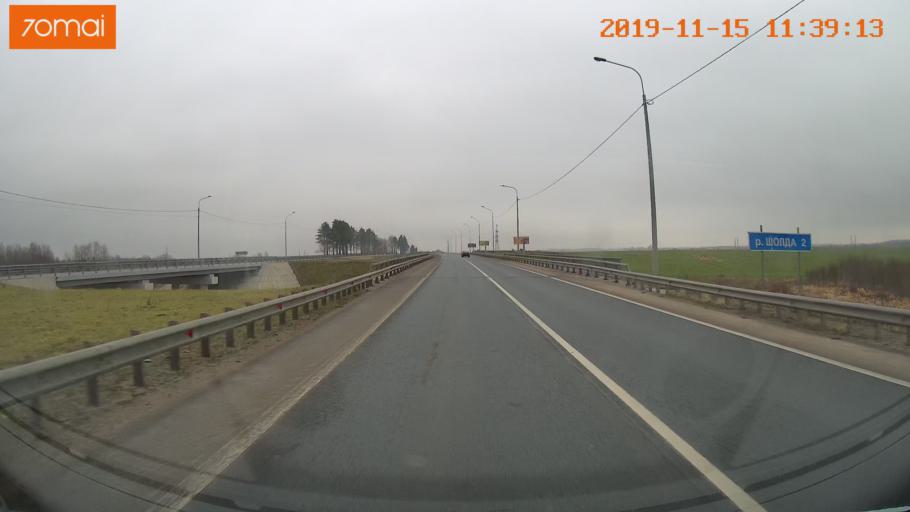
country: RU
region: Vologda
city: Molochnoye
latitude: 59.2110
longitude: 39.7180
